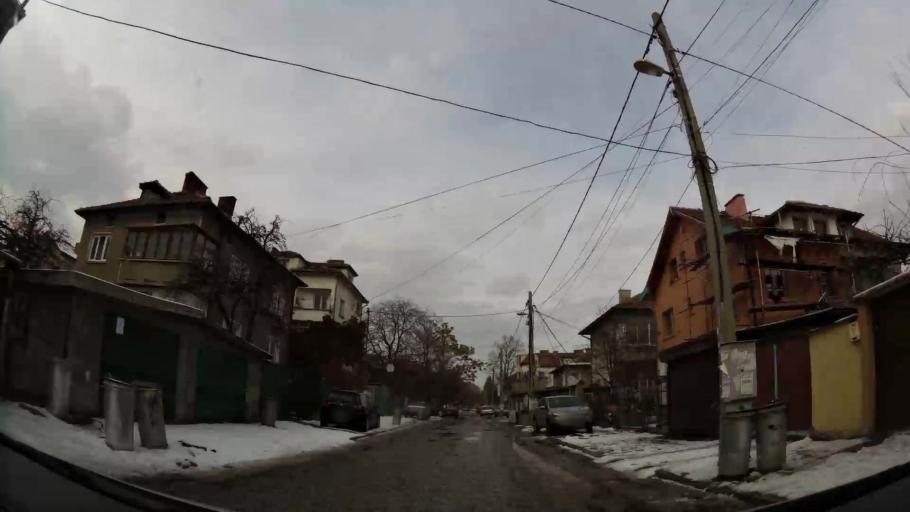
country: BG
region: Sofia-Capital
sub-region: Stolichna Obshtina
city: Sofia
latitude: 42.7034
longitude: 23.3802
